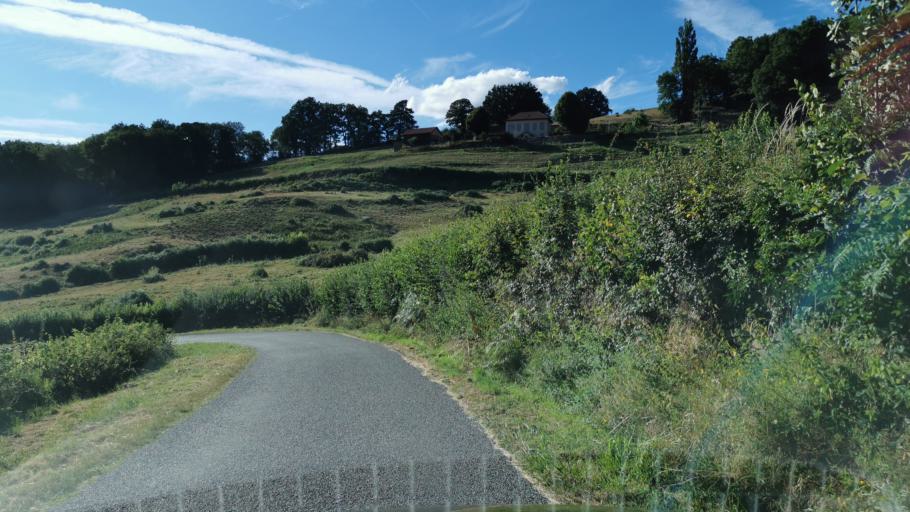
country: FR
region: Bourgogne
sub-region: Departement de Saone-et-Loire
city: Marmagne
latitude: 46.8730
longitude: 4.3356
